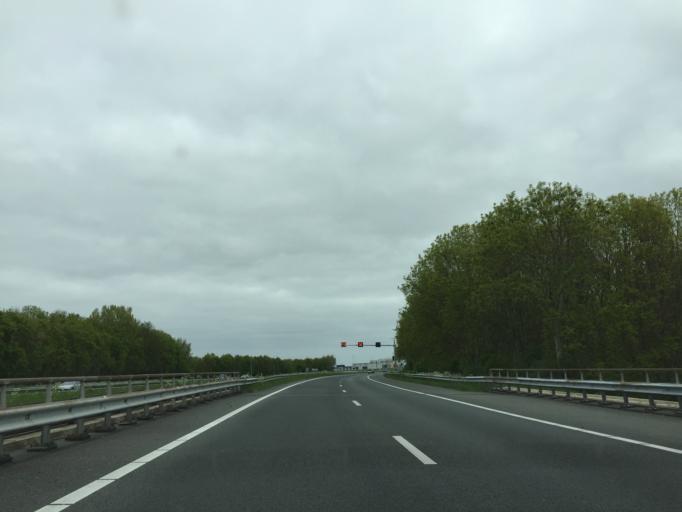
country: NL
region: North Holland
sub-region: Gemeente Hollands Kroon
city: Den Oever
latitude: 52.9288
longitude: 5.0354
